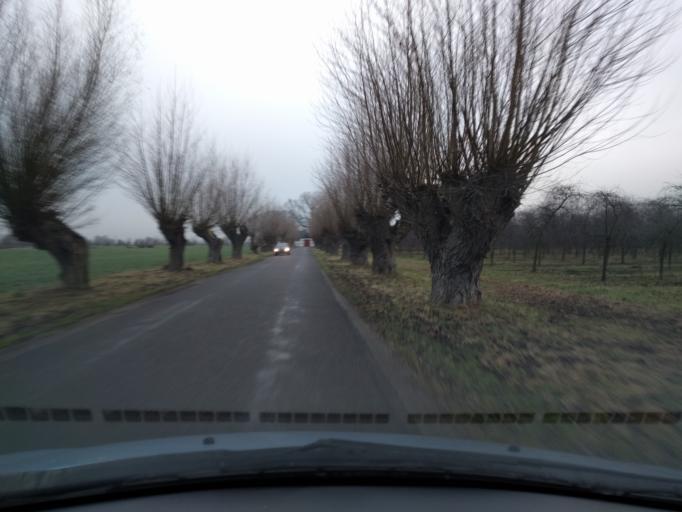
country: DK
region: South Denmark
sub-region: Kerteminde Kommune
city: Munkebo
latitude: 55.4220
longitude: 10.5257
